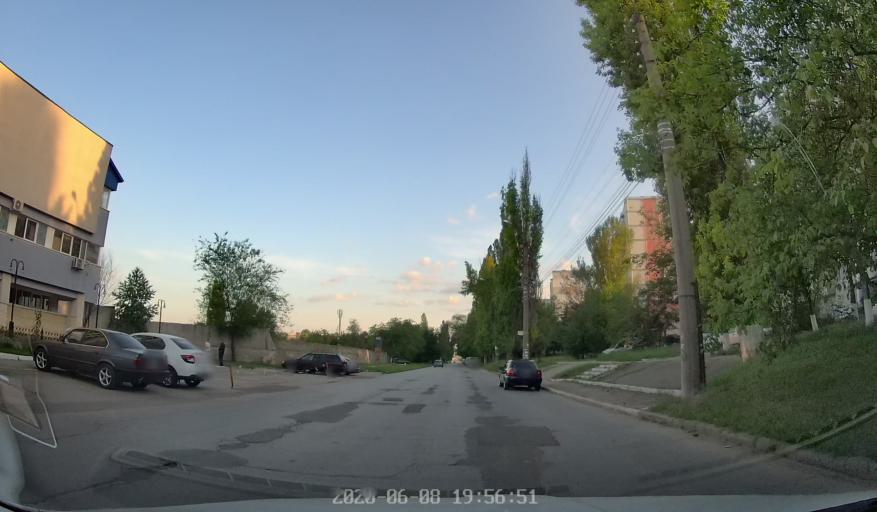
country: MD
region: Chisinau
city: Chisinau
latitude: 47.0195
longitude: 28.8828
